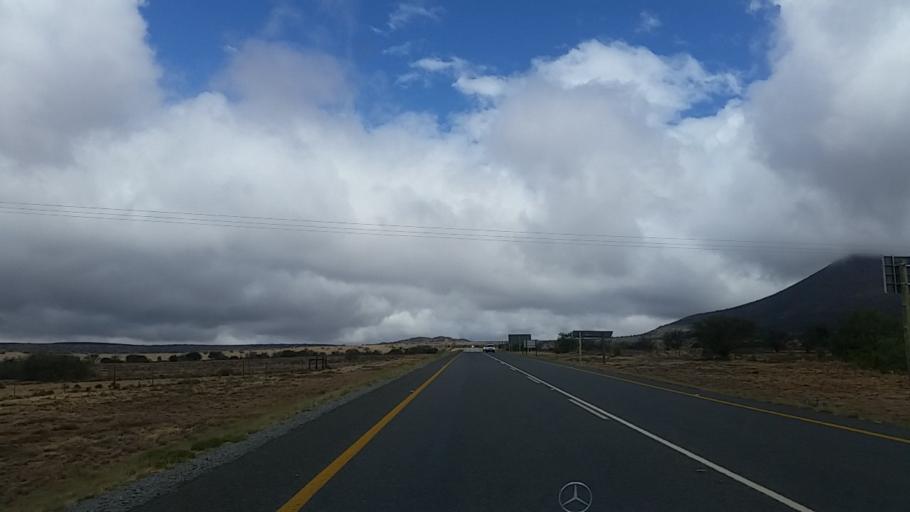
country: ZA
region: Eastern Cape
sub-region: Cacadu District Municipality
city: Graaff-Reinet
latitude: -32.0319
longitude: 24.6256
